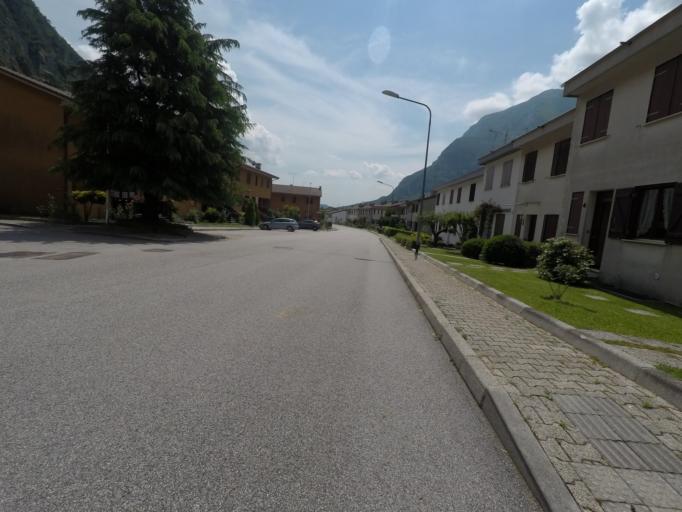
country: IT
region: Friuli Venezia Giulia
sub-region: Provincia di Udine
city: Venzone
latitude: 46.3703
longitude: 13.1338
